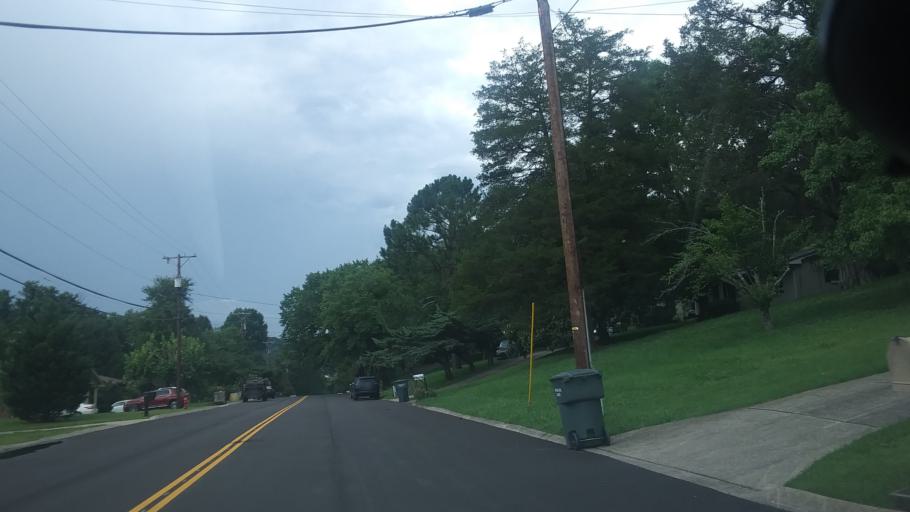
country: US
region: Tennessee
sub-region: Davidson County
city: Belle Meade
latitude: 36.0819
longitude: -86.9372
